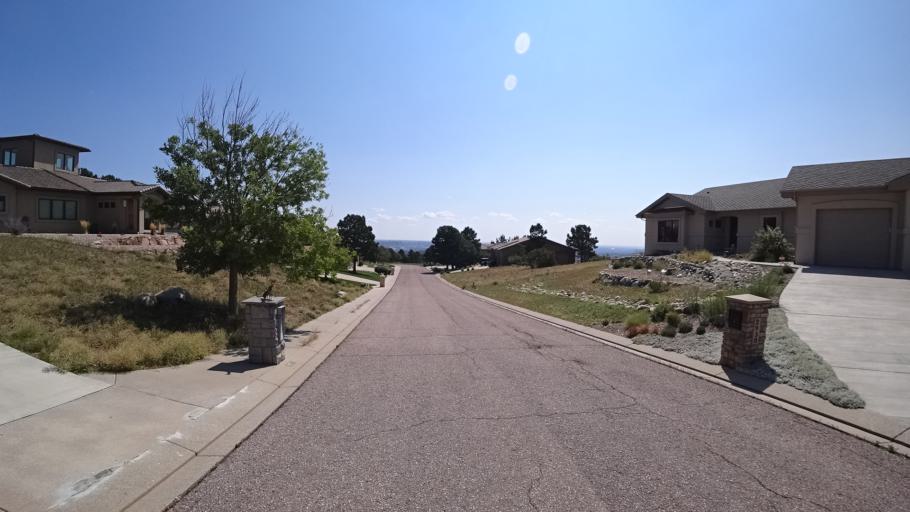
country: US
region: Colorado
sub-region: El Paso County
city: Manitou Springs
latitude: 38.9191
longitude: -104.8818
